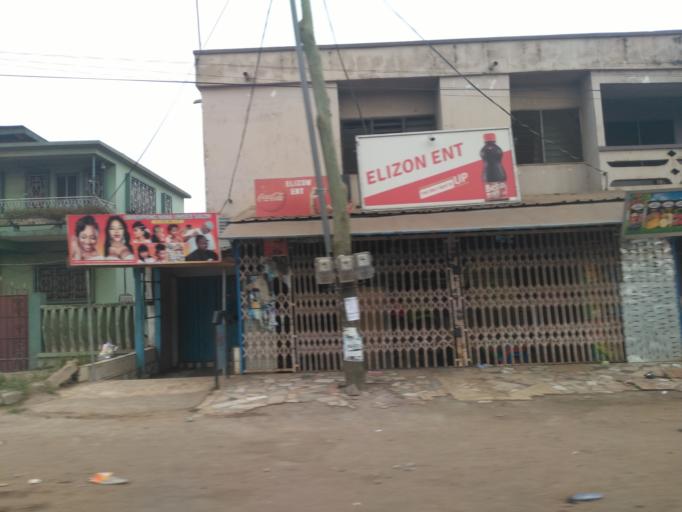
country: GH
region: Ashanti
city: Tafo
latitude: 6.7141
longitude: -1.6082
